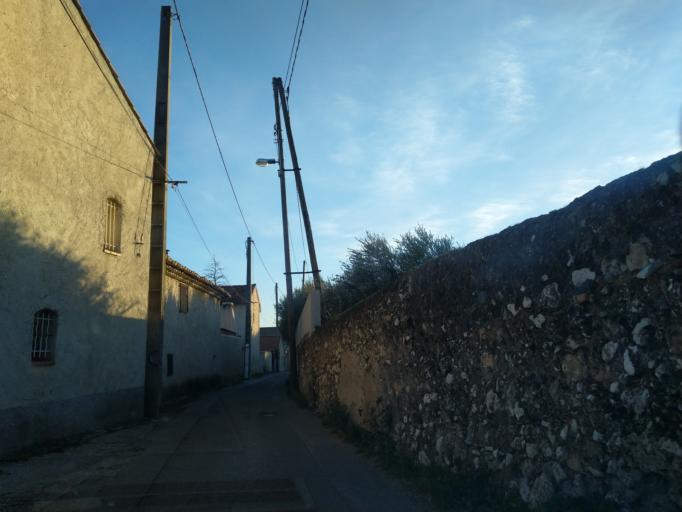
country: FR
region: Provence-Alpes-Cote d'Azur
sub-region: Departement des Bouches-du-Rhone
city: Plan-de-Cuques
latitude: 43.3412
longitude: 5.4510
